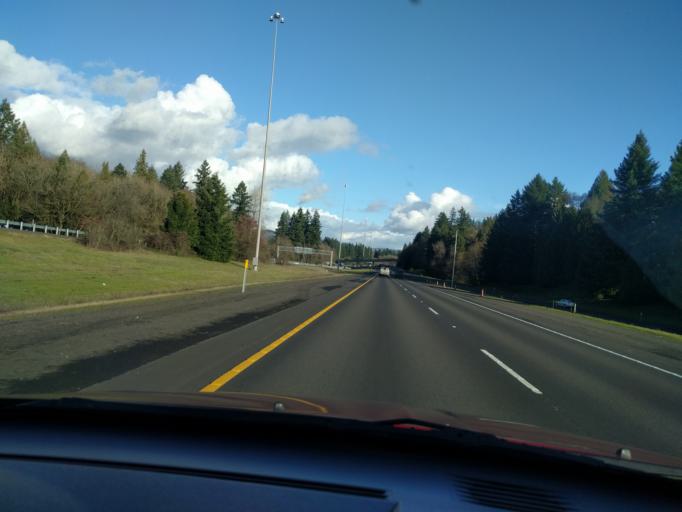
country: US
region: Oregon
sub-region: Washington County
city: Tualatin
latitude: 45.3696
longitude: -122.7519
